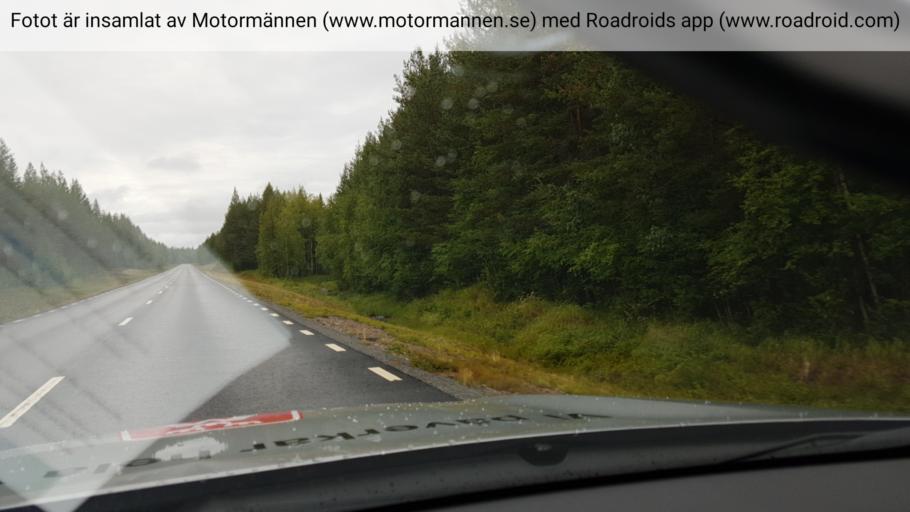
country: SE
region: Norrbotten
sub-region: Alvsbyns Kommun
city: AElvsbyn
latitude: 66.2532
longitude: 20.8497
